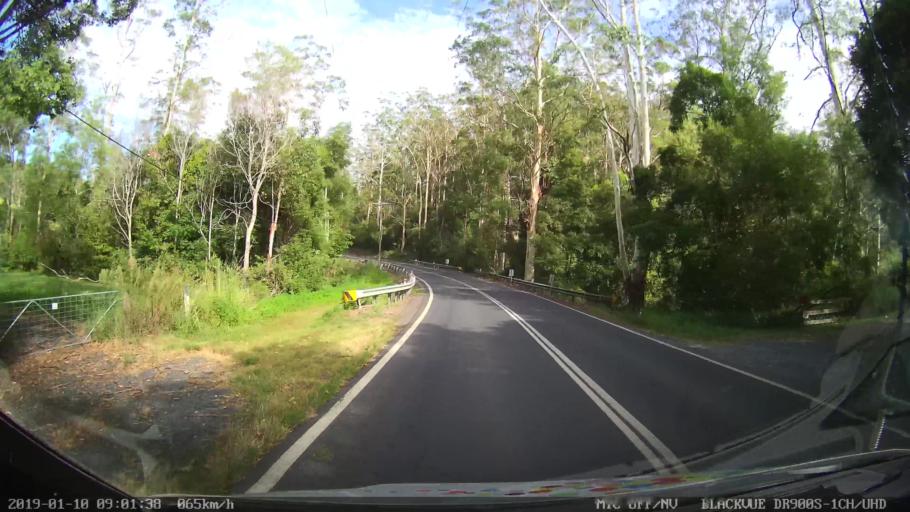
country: AU
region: New South Wales
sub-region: Coffs Harbour
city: Coffs Harbour
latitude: -30.2769
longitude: 153.0600
